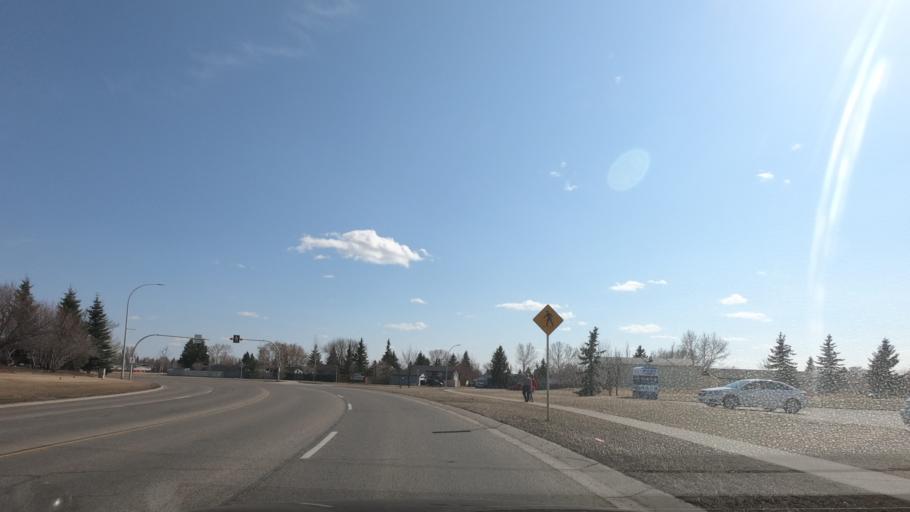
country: CA
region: Alberta
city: Airdrie
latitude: 51.2848
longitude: -113.9962
